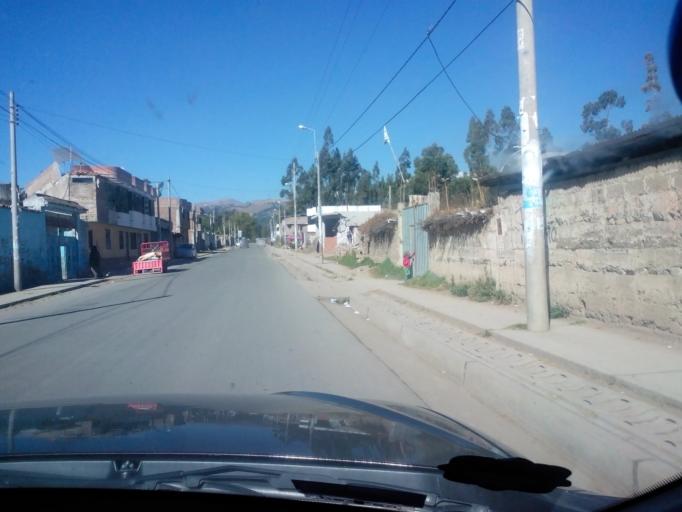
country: PE
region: Apurimac
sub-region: Provincia de Andahuaylas
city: Talavera
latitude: -13.6587
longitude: -73.4288
